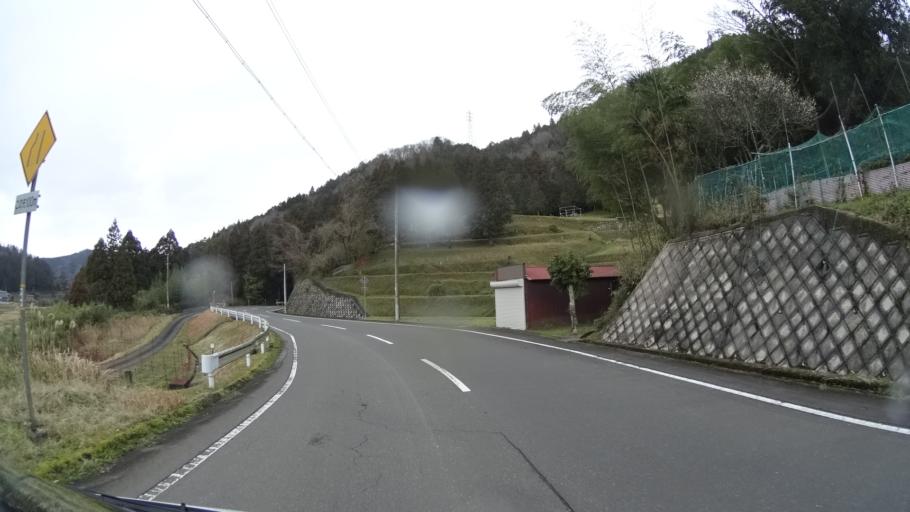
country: JP
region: Kyoto
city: Ayabe
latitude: 35.3288
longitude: 135.3542
